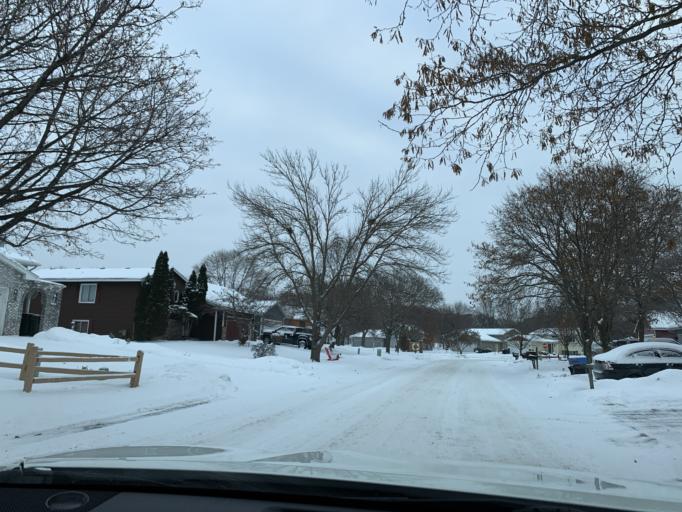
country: US
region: Minnesota
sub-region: Anoka County
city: Coon Rapids
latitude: 45.1647
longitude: -93.2830
